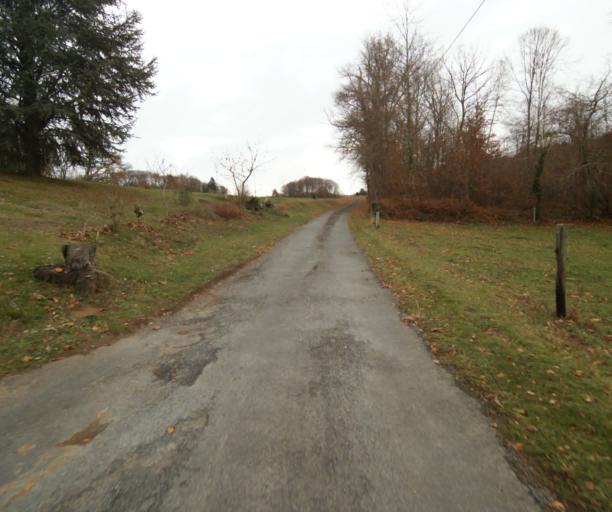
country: FR
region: Limousin
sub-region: Departement de la Correze
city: Chameyrat
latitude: 45.2535
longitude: 1.6714
